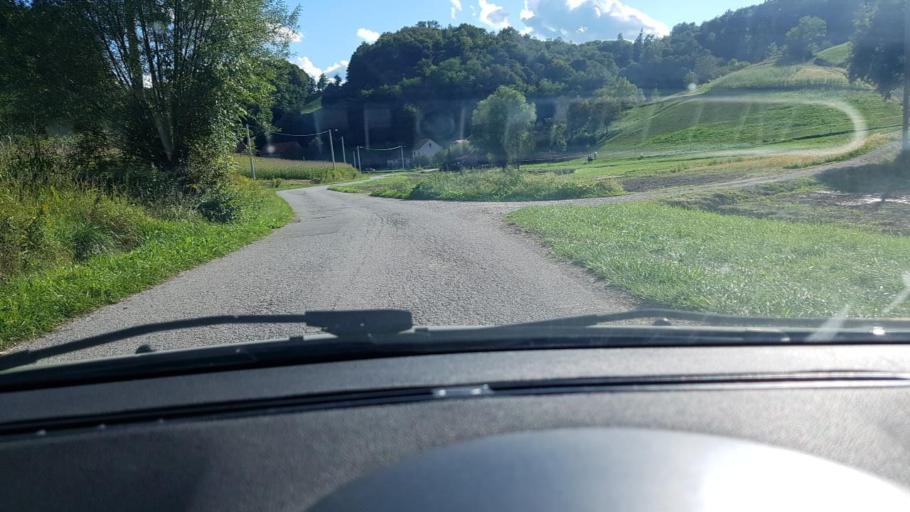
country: HR
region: Krapinsko-Zagorska
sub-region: Grad Krapina
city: Krapina
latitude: 46.1417
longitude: 15.8374
